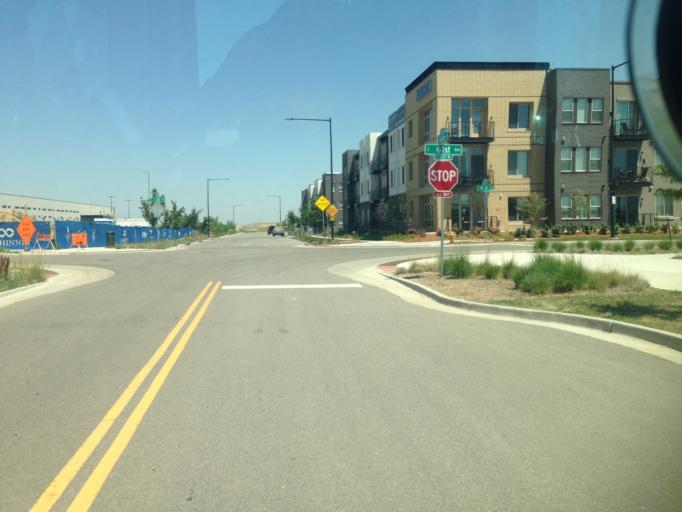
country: US
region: Colorado
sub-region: Adams County
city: Aurora
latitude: 39.8071
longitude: -104.7796
